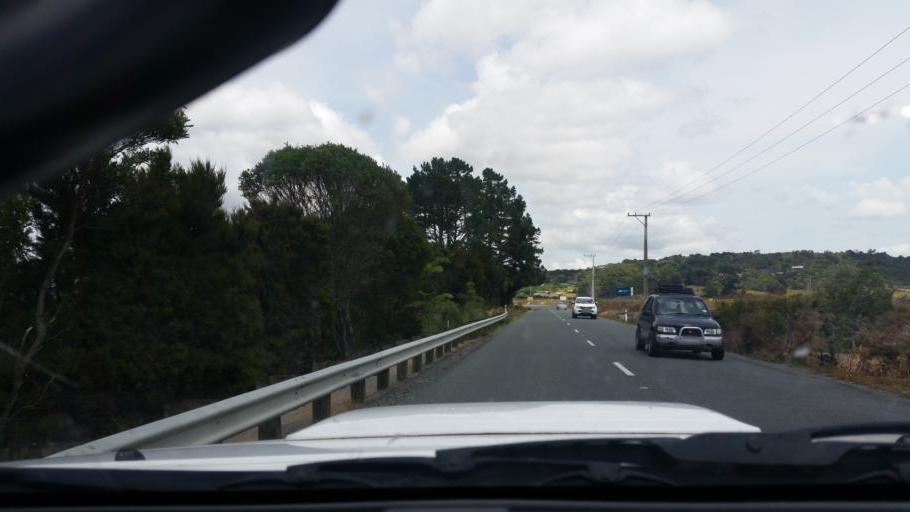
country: NZ
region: Auckland
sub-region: Auckland
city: Wellsford
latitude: -36.1101
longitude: 174.5776
